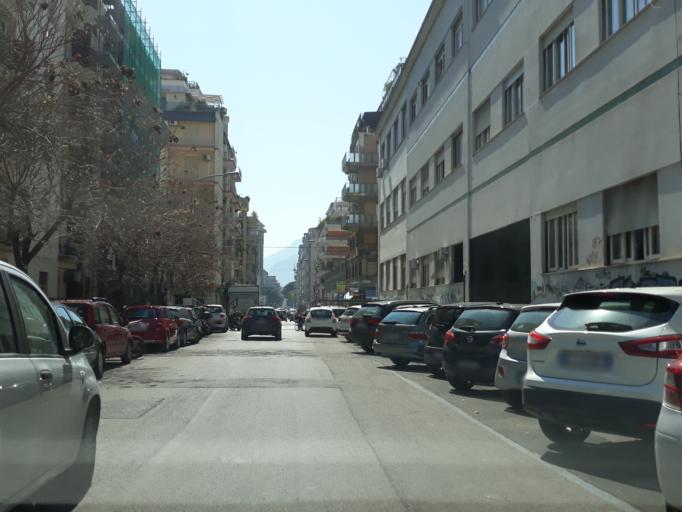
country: IT
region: Sicily
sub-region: Palermo
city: Palermo
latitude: 38.1375
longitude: 13.3515
